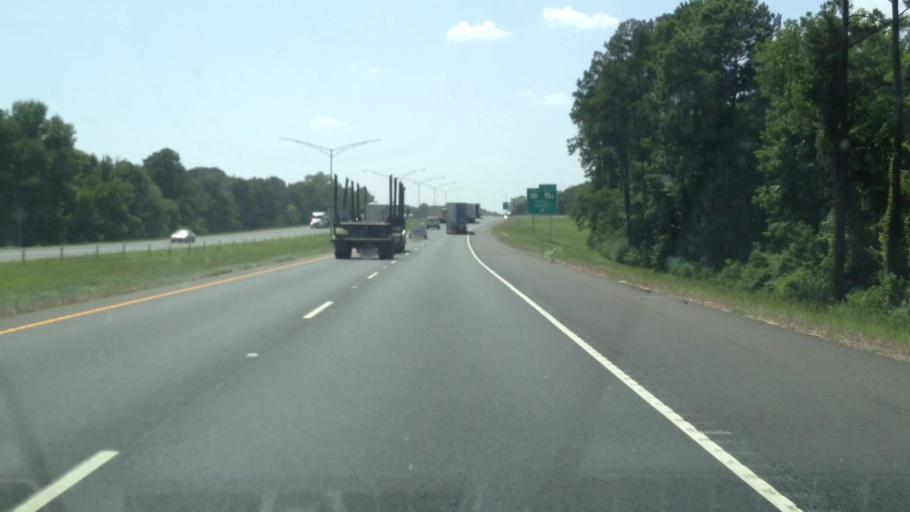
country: US
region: Louisiana
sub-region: Webster Parish
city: Minden
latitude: 32.5883
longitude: -93.2865
